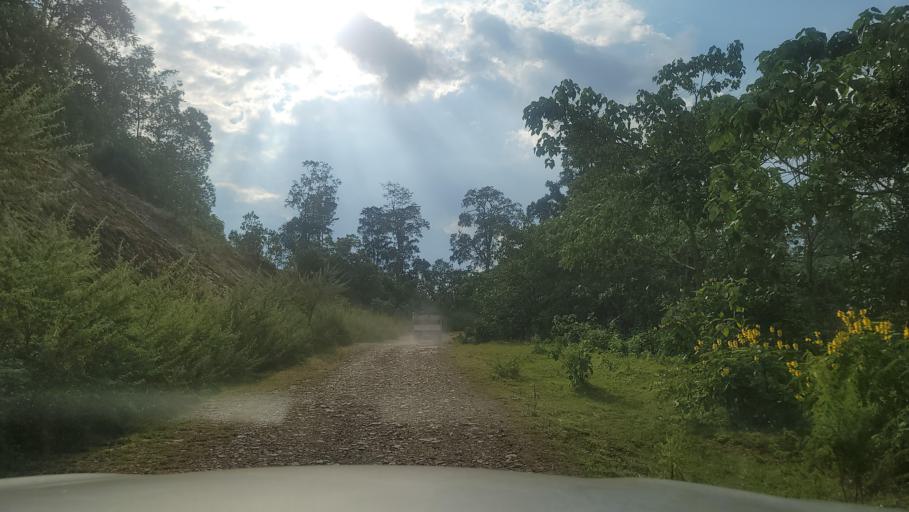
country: ET
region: Southern Nations, Nationalities, and People's Region
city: Bonga
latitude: 7.5768
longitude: 36.1627
